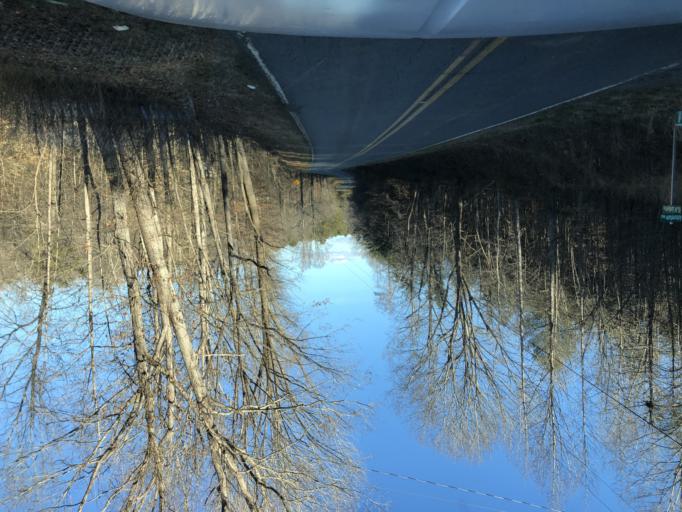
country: US
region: North Carolina
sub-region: Cleveland County
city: Shelby
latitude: 35.3259
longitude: -81.5397
